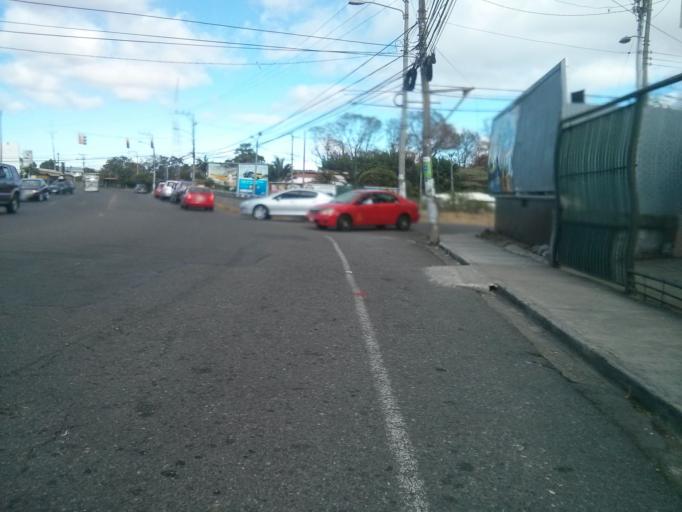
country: CR
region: San Jose
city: San Pedro
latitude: 9.9247
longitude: -84.0561
